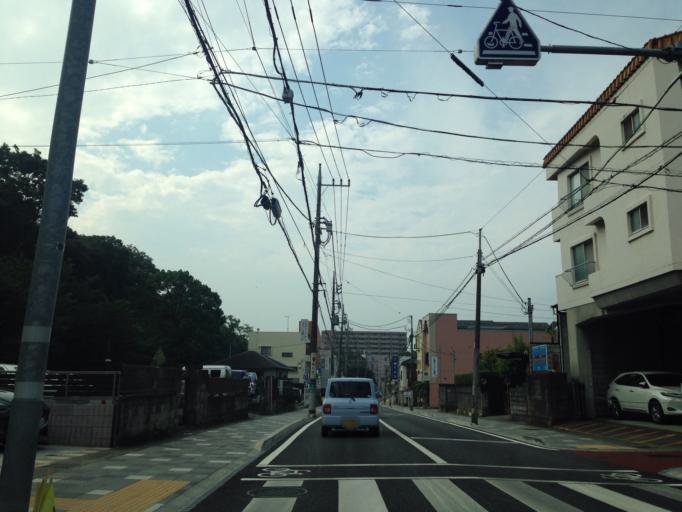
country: JP
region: Shizuoka
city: Mishima
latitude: 35.1230
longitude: 138.9177
